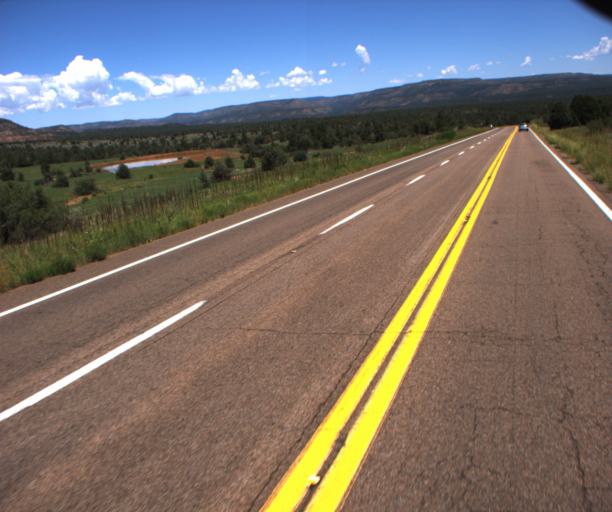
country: US
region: Arizona
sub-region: Navajo County
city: Cibecue
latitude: 33.9698
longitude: -110.3181
